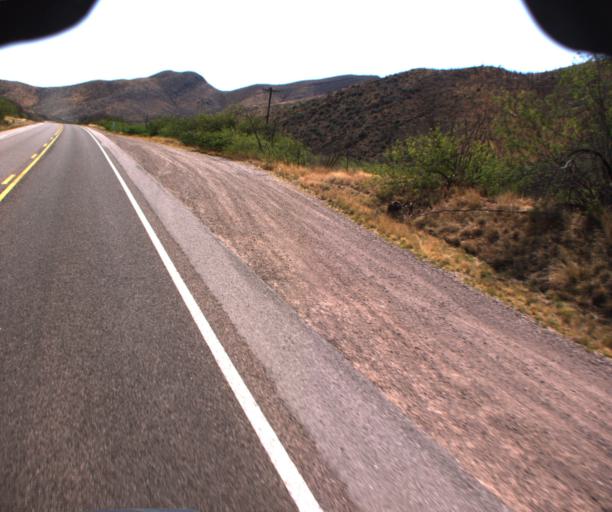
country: US
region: Arizona
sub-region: Cochise County
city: Bisbee
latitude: 31.4312
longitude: -109.8553
